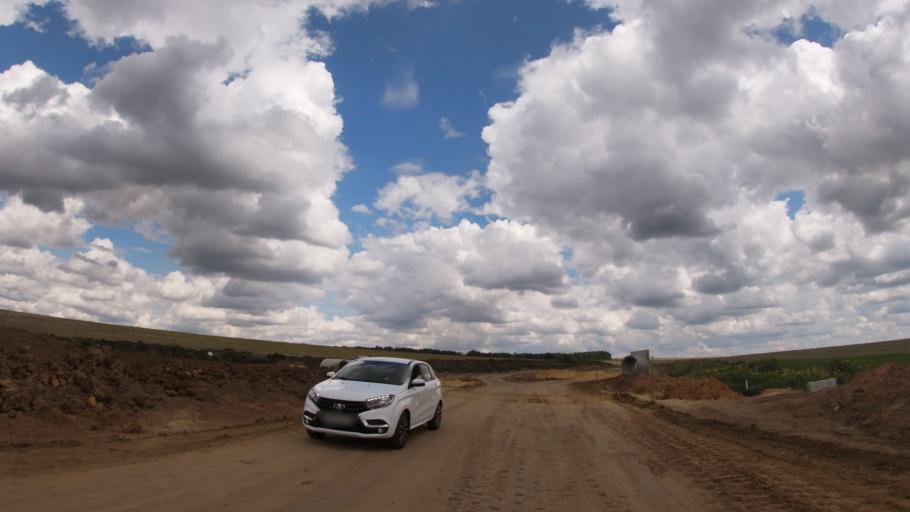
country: RU
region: Belgorod
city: Mayskiy
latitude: 50.5184
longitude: 36.4934
